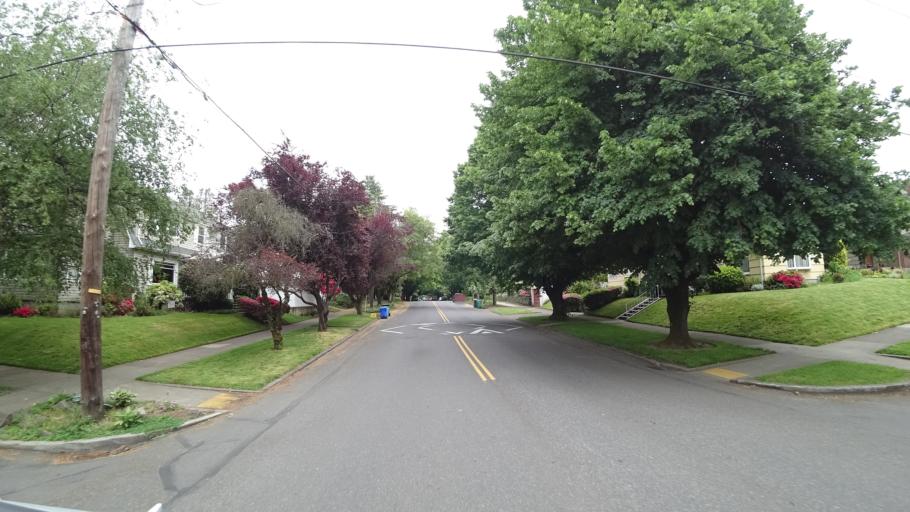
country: US
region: Oregon
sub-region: Multnomah County
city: Portland
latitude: 45.5421
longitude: -122.6525
